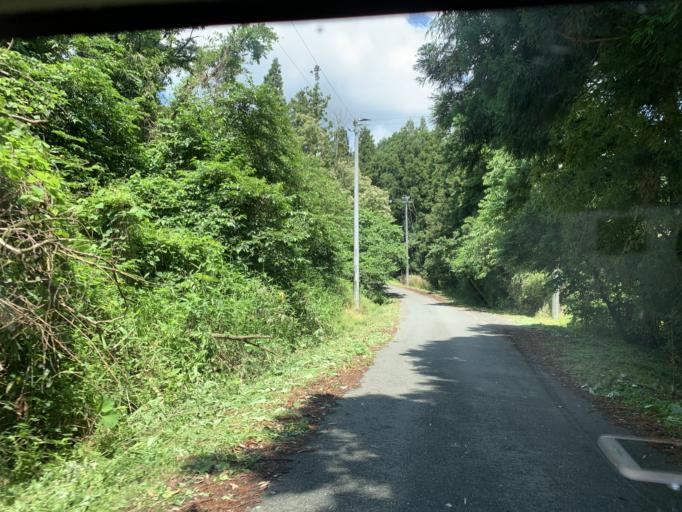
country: JP
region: Iwate
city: Ichinoseki
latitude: 38.9258
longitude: 141.0520
